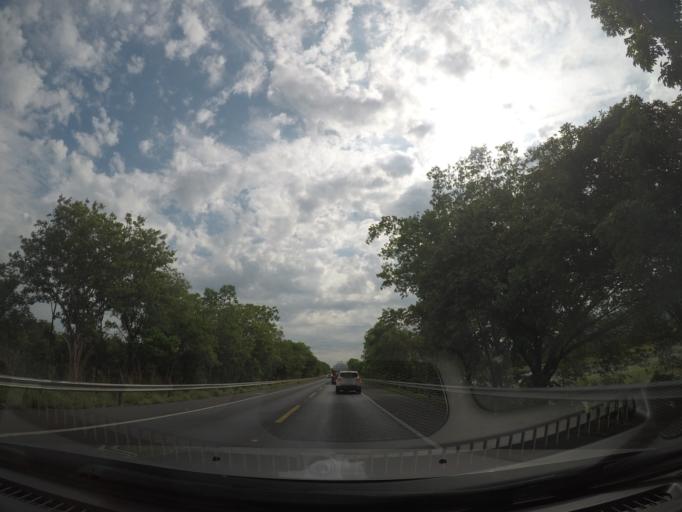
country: BR
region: Goias
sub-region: Formosa
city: Formosa
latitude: -14.9171
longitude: -46.9547
